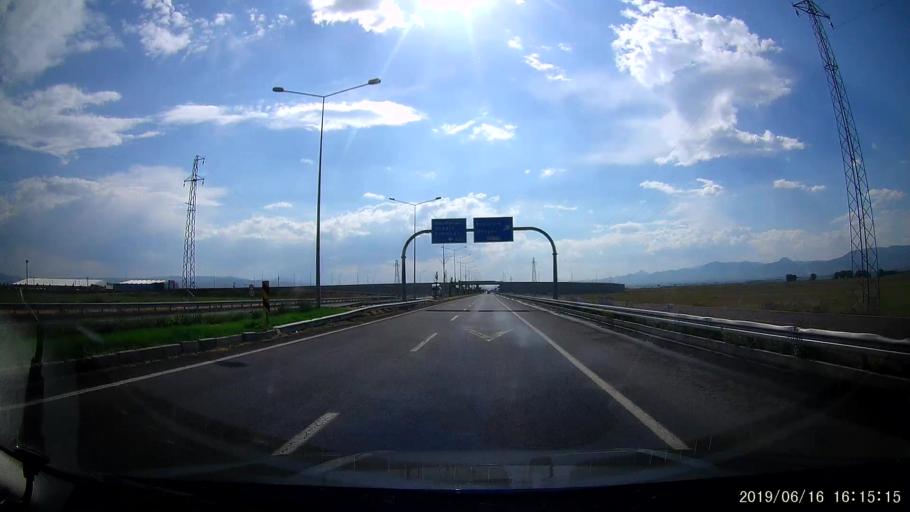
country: TR
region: Erzurum
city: Erzurum
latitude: 39.9617
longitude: 41.2303
